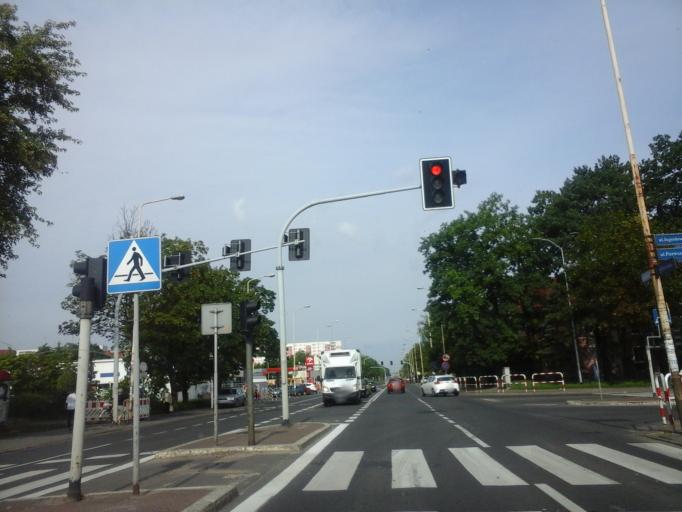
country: PL
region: West Pomeranian Voivodeship
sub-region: Powiat stargardzki
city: Stargard Szczecinski
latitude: 53.3398
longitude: 15.0201
